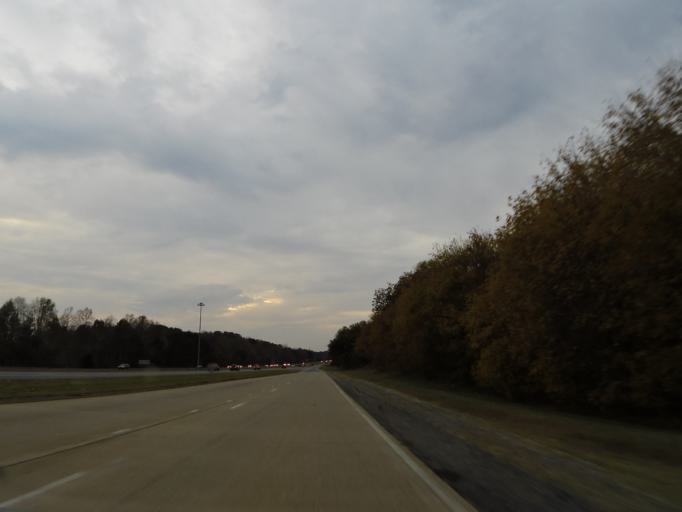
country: US
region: North Carolina
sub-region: Catawba County
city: Mountain View
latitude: 35.7077
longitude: -81.3588
